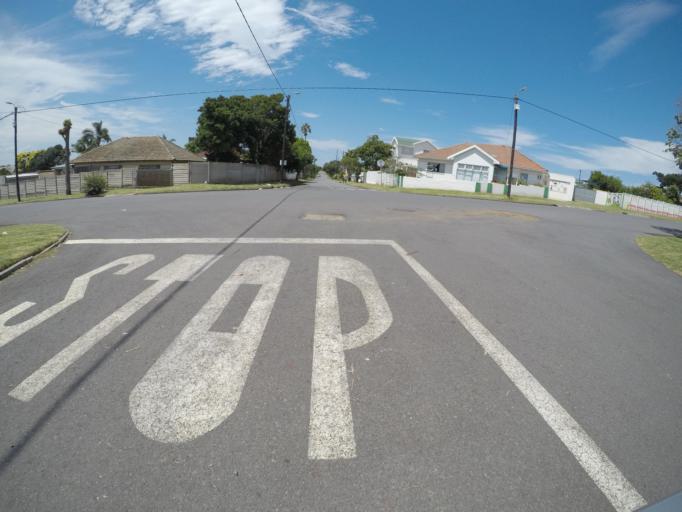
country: ZA
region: Eastern Cape
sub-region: Buffalo City Metropolitan Municipality
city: East London
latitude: -33.0333
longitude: 27.8595
